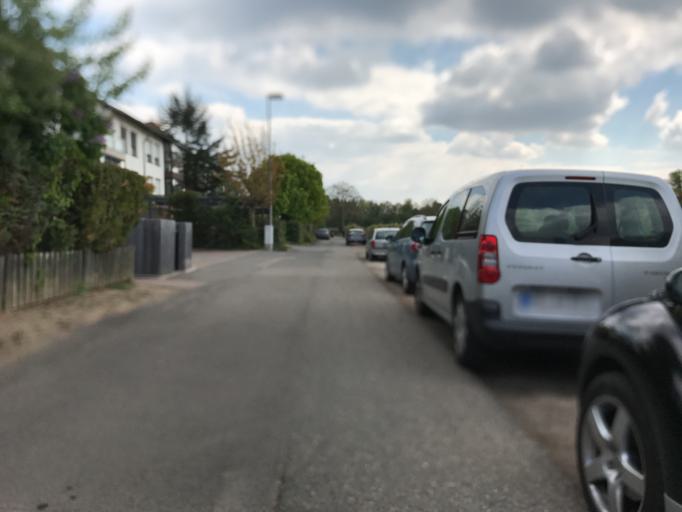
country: DE
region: Rheinland-Pfalz
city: Mainz
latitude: 49.9844
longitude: 8.2579
